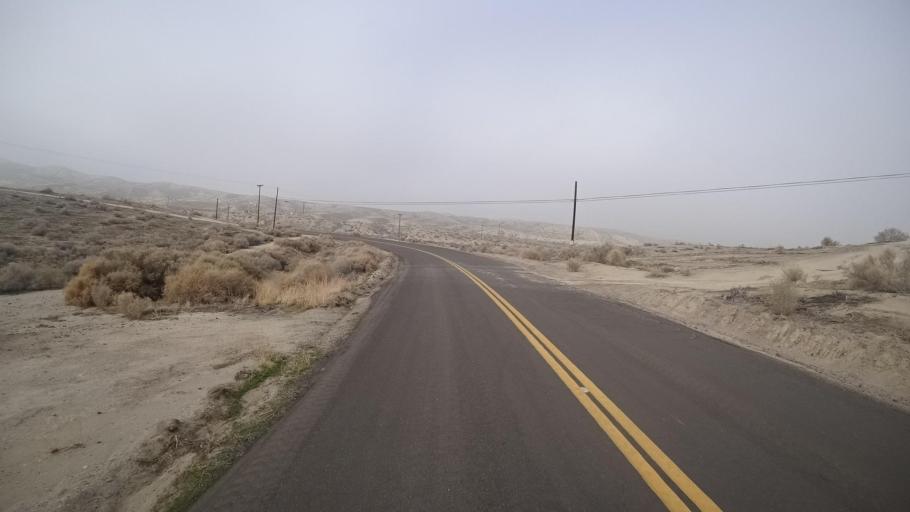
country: US
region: California
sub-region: Kern County
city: Ford City
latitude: 35.1663
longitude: -119.3931
